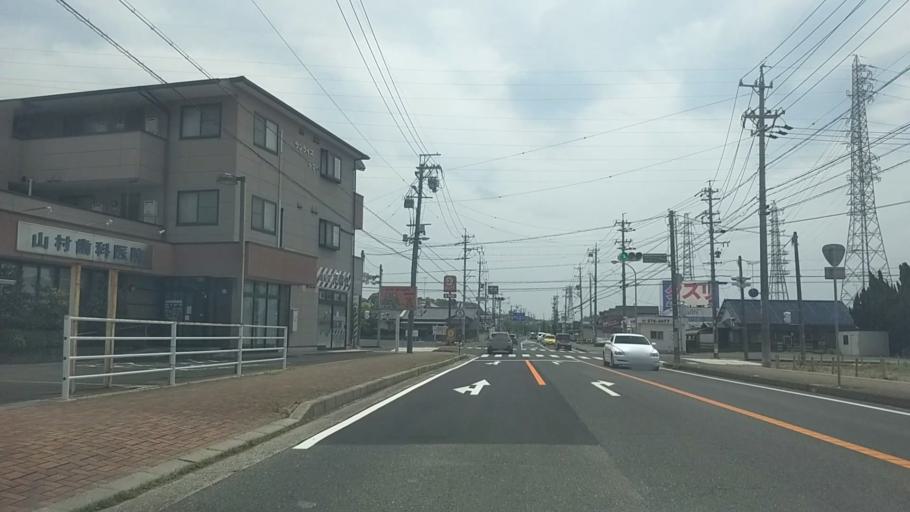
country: JP
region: Shizuoka
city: Kosai-shi
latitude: 34.7189
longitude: 137.5331
